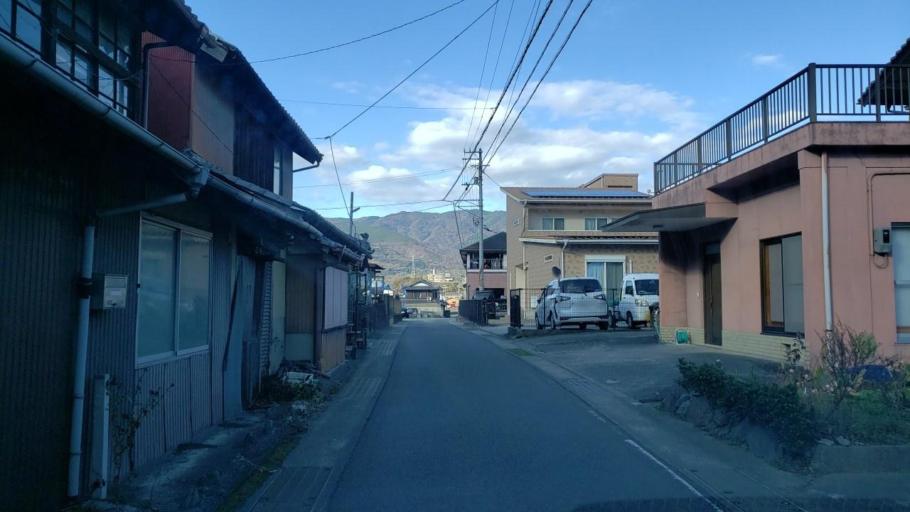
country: JP
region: Tokushima
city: Wakimachi
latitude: 34.0301
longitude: 134.0295
